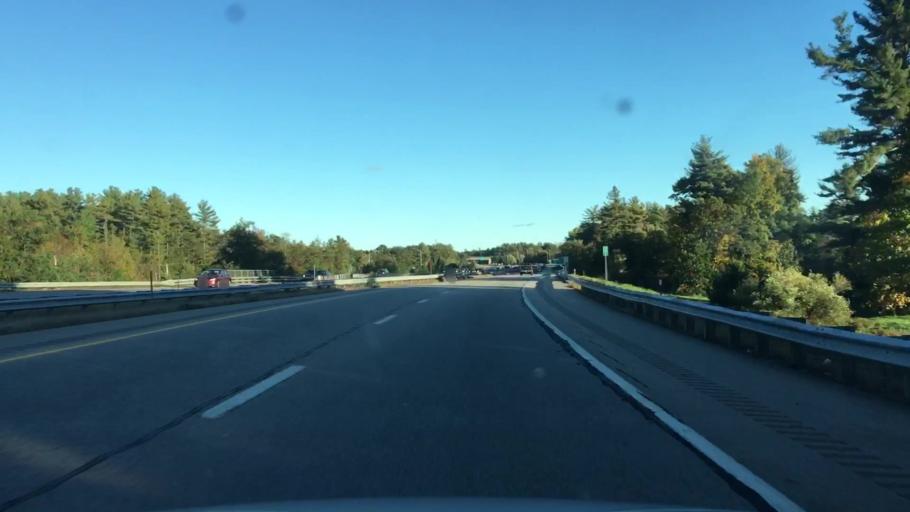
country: US
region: New Hampshire
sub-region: Rockingham County
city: Exeter
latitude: 43.0064
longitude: -70.9880
